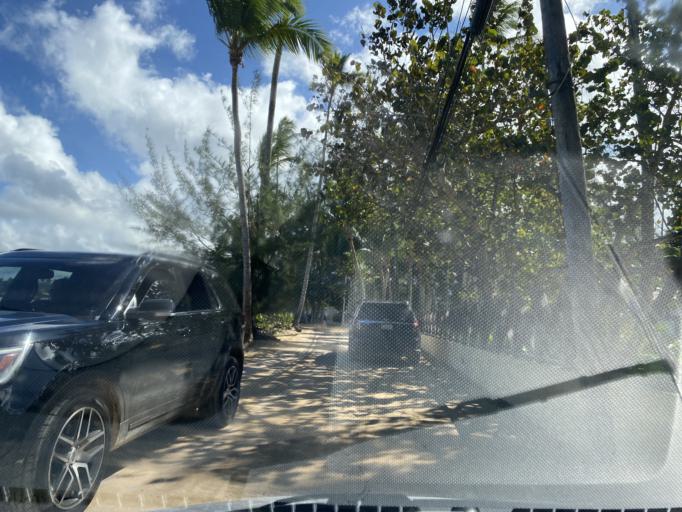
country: DO
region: Samana
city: Las Terrenas
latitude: 19.3242
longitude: -69.5433
